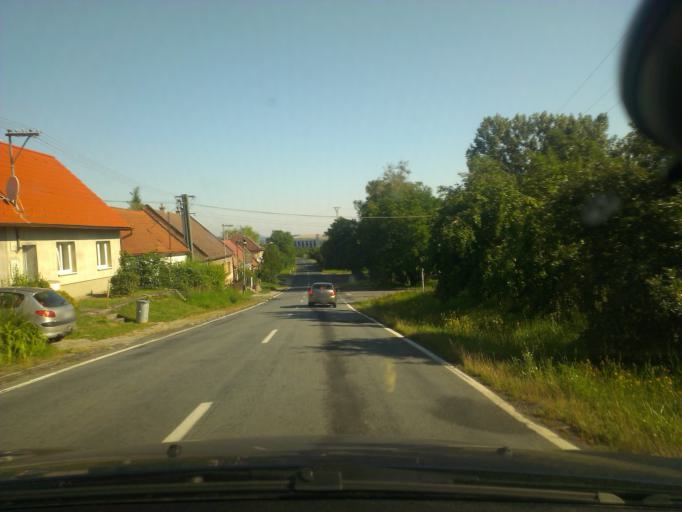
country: CZ
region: South Moravian
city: Velka nad Velickou
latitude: 48.8617
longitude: 17.5226
